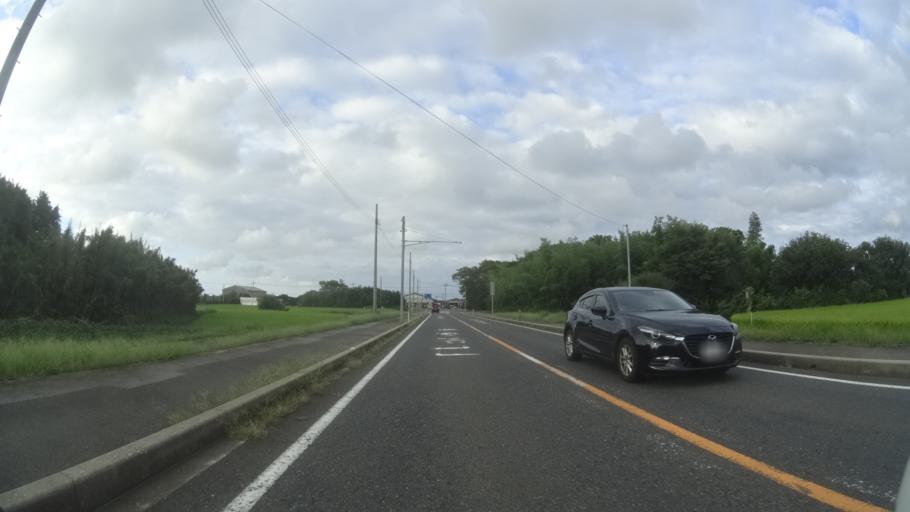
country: JP
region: Tottori
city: Kurayoshi
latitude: 35.5196
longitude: 133.5990
